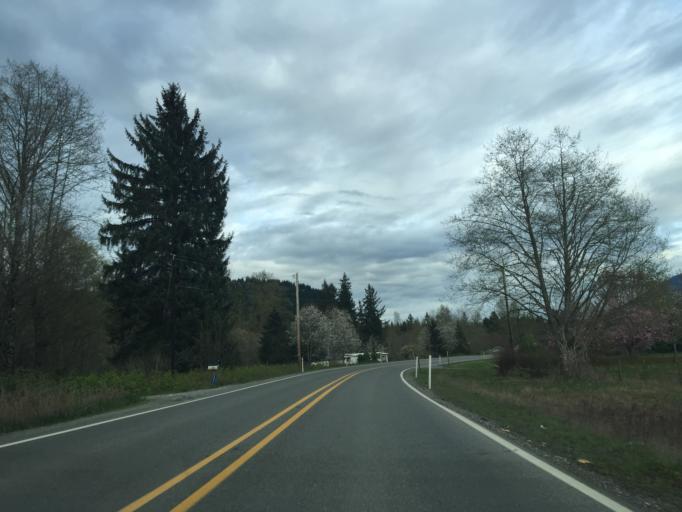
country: US
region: Washington
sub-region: Snohomish County
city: Arlington Heights
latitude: 48.2748
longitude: -121.9076
